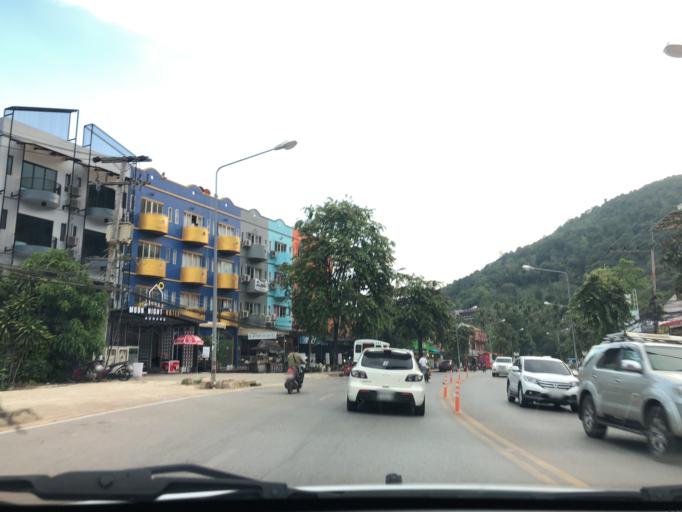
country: TH
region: Phangnga
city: Ban Ao Nang
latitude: 8.0392
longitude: 98.8350
